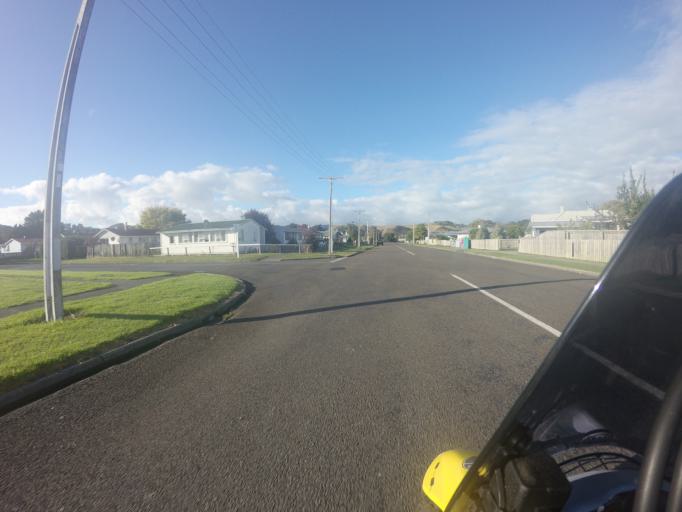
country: NZ
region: Gisborne
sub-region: Gisborne District
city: Gisborne
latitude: -38.6713
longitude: 178.0512
